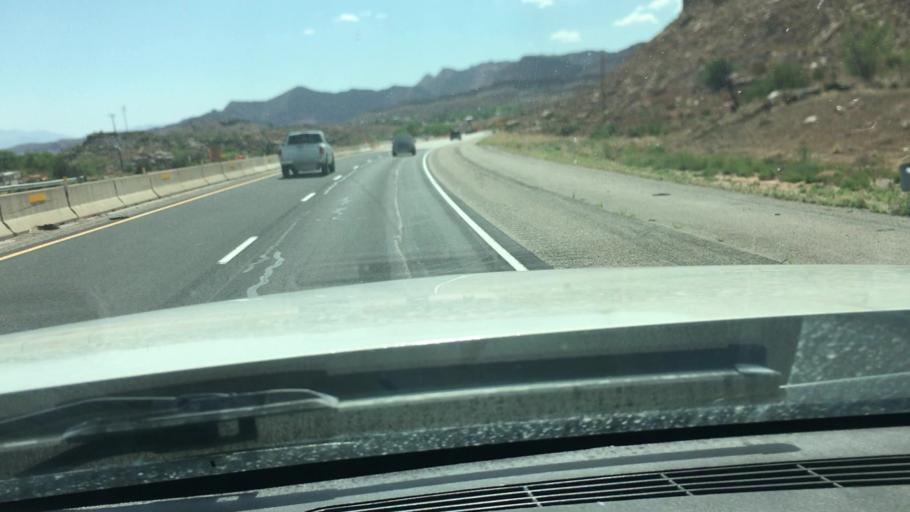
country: US
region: Utah
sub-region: Washington County
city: Toquerville
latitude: 37.2429
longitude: -113.3558
